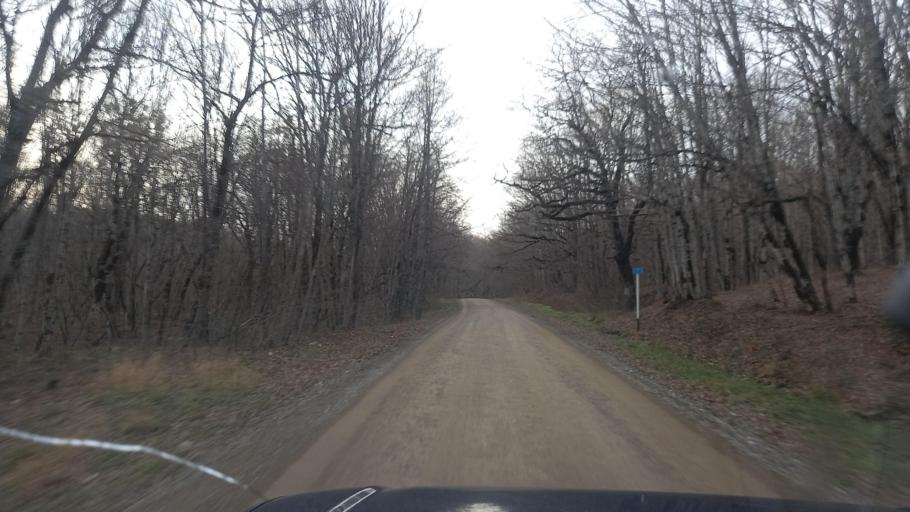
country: RU
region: Krasnodarskiy
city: Agoy
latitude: 44.3498
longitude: 39.2277
